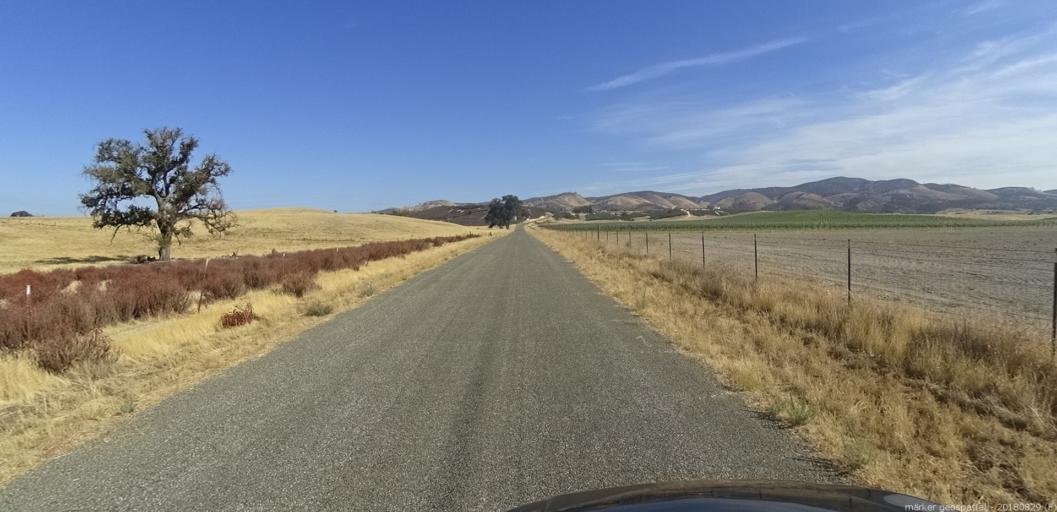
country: US
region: California
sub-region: Monterey County
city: King City
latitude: 35.9685
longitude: -121.1175
